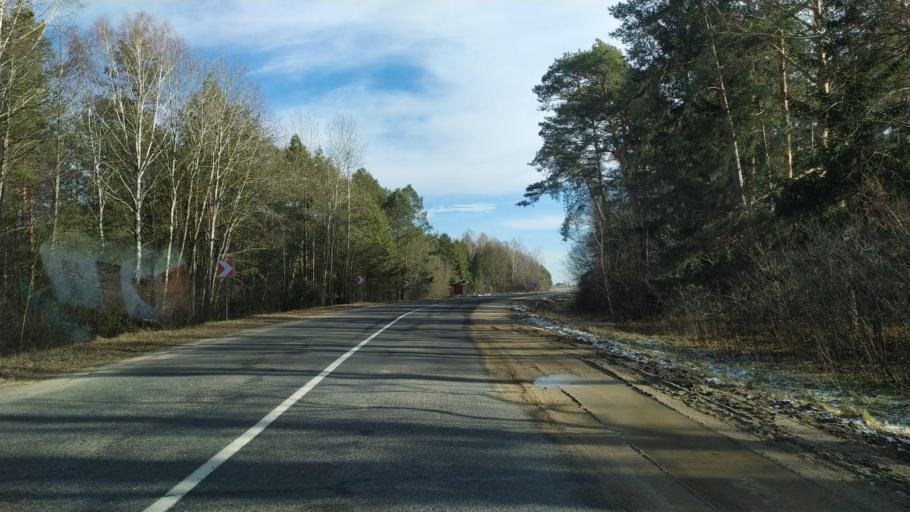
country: BY
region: Brest
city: Pruzhany
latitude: 52.5767
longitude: 24.2991
